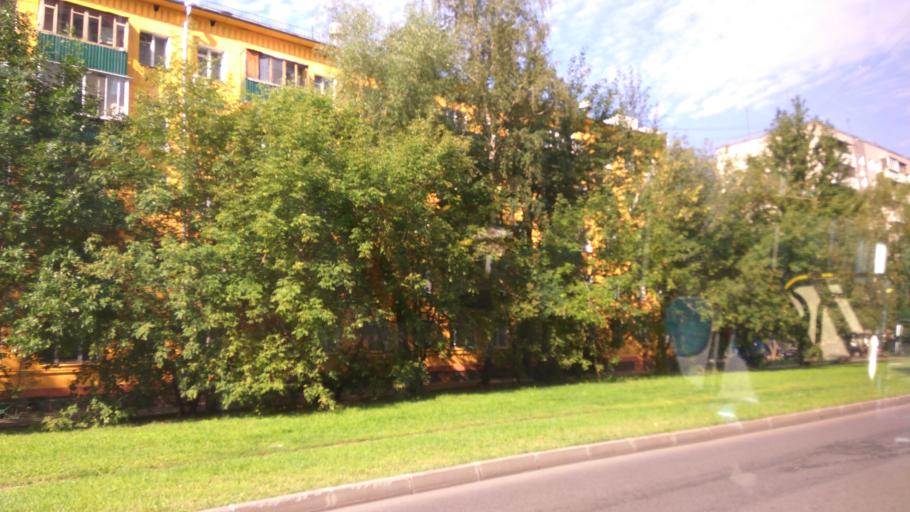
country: RU
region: Moscow
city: Lefortovo
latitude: 55.7658
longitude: 37.7388
